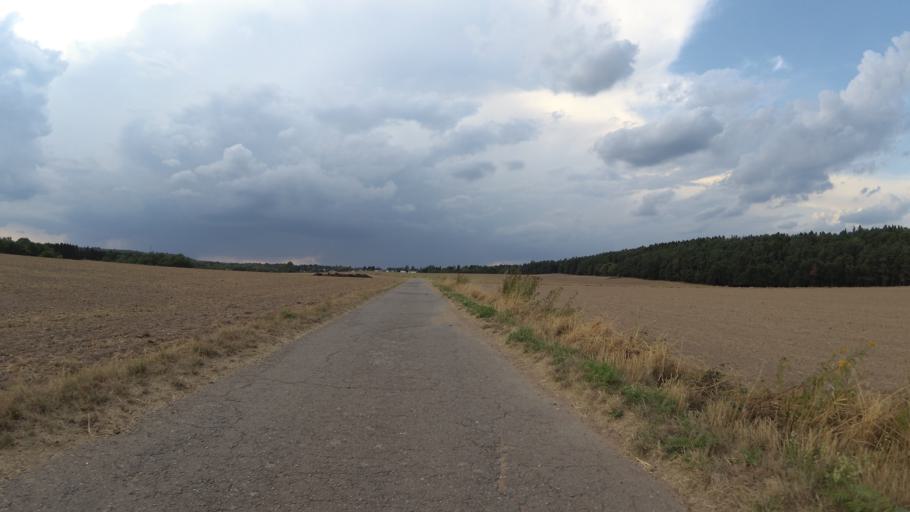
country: DE
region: Saarland
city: Bexbach
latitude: 49.3183
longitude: 7.2580
